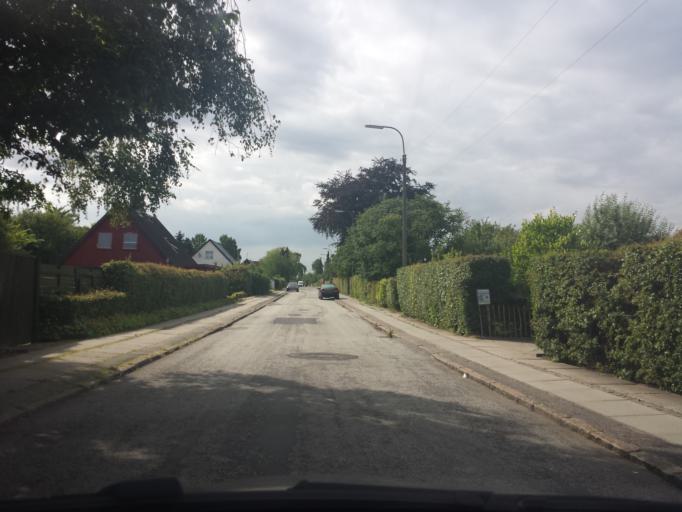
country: DK
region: Capital Region
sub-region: Herlev Kommune
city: Herlev
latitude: 55.7233
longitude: 12.4027
